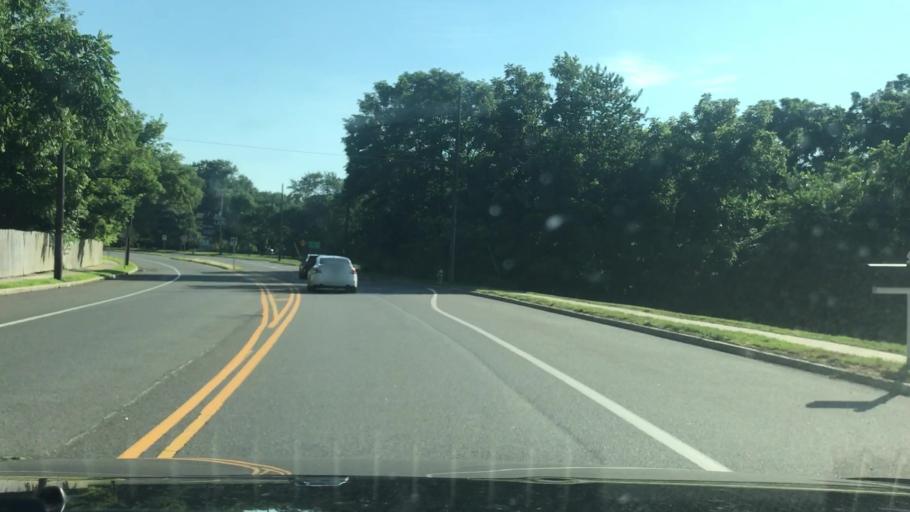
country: US
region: New Jersey
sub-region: Ocean County
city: Leisure Village
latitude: 40.0137
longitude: -74.2008
